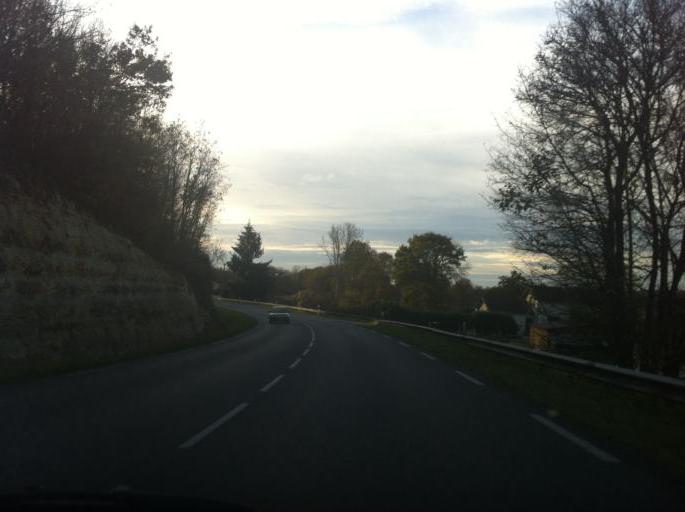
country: FR
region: Aquitaine
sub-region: Departement de la Dordogne
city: Tocane-Saint-Apre
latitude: 45.2581
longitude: 0.5072
